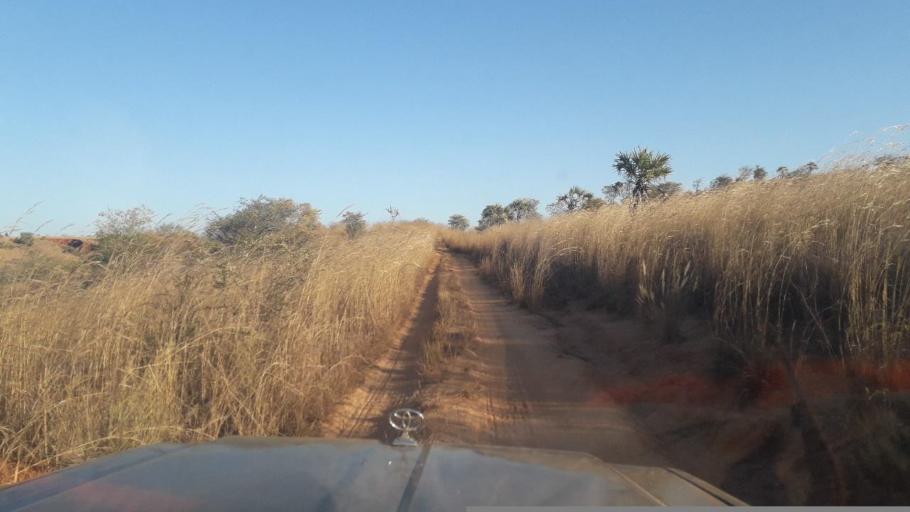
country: MG
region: Boeny
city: Sitampiky
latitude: -16.4956
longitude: 45.6076
